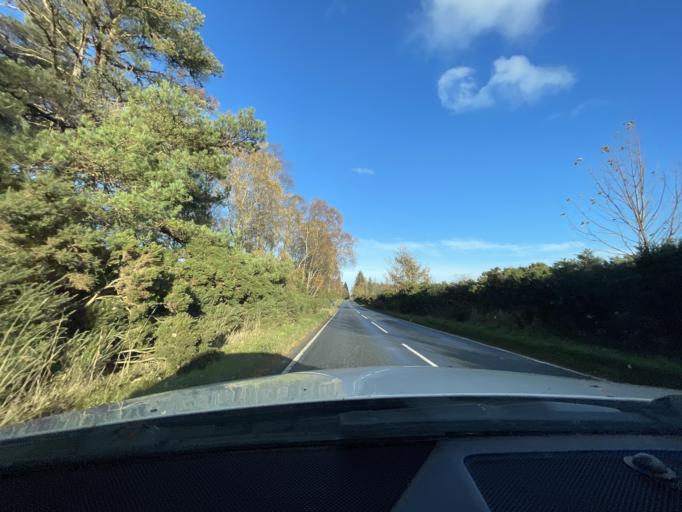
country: GB
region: Scotland
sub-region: Highland
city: Inverness
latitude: 57.4132
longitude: -4.3060
